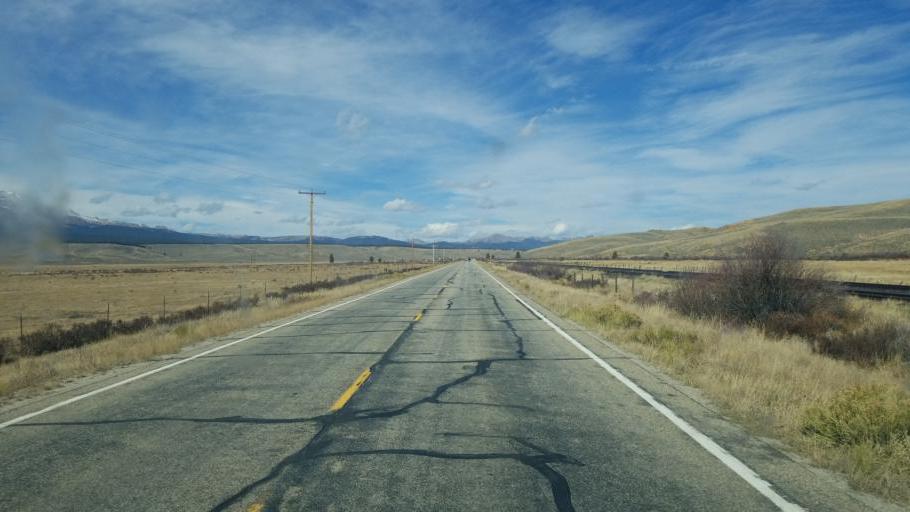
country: US
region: Colorado
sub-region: Lake County
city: Leadville
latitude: 39.1141
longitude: -106.3056
